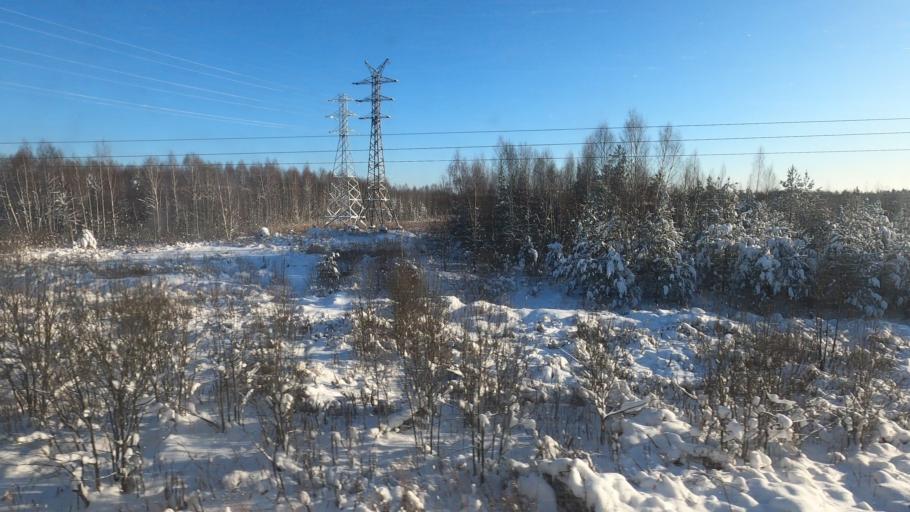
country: RU
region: Moskovskaya
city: Zhukovka
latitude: 56.4678
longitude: 37.5267
